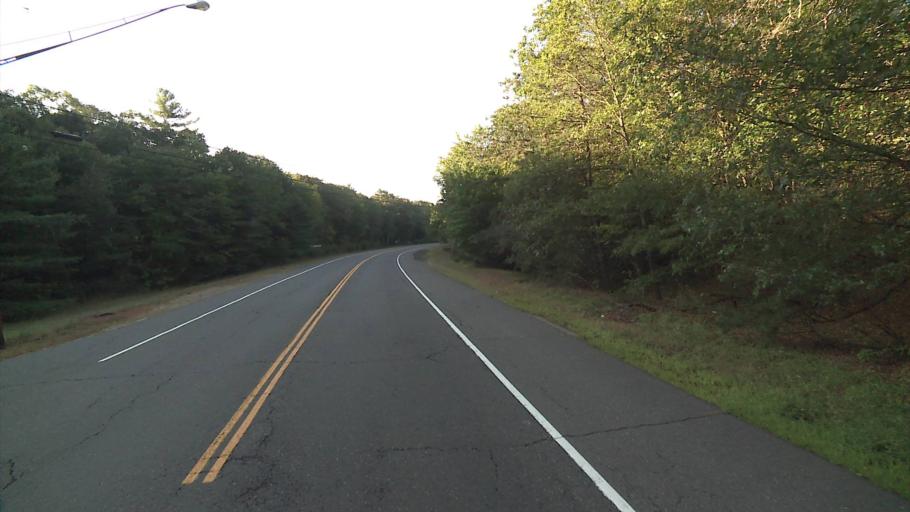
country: US
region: Connecticut
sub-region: Tolland County
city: Mansfield City
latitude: 41.7504
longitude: -72.2605
